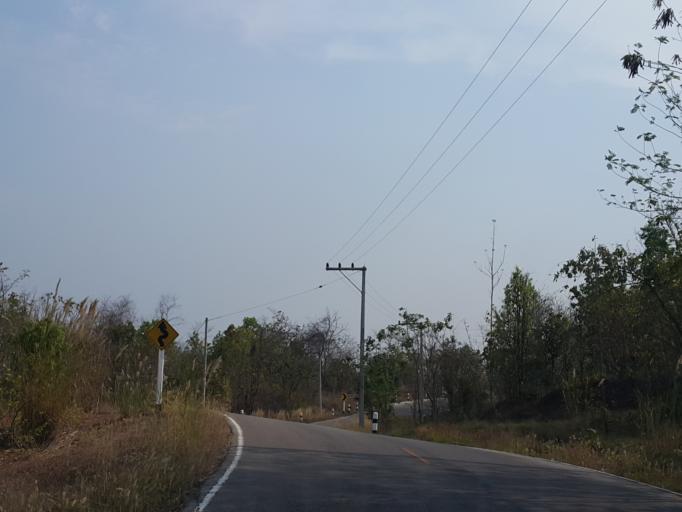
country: TH
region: Lampang
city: Chae Hom
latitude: 18.7320
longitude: 99.5464
